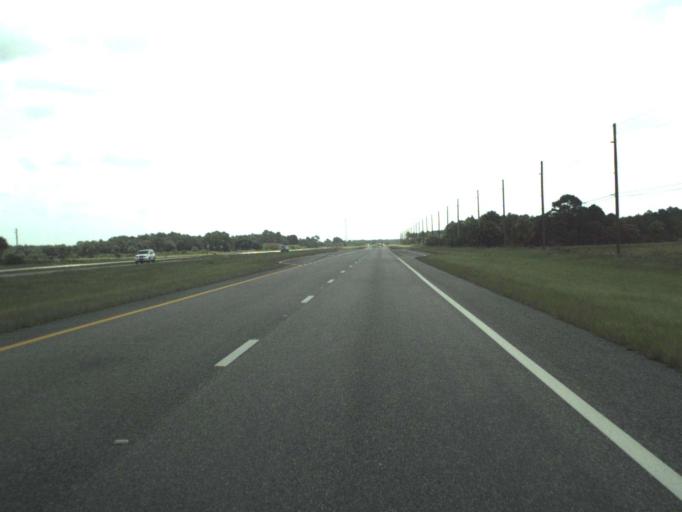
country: US
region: Florida
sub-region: Okeechobee County
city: Taylor Creek
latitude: 27.3668
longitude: -80.6049
